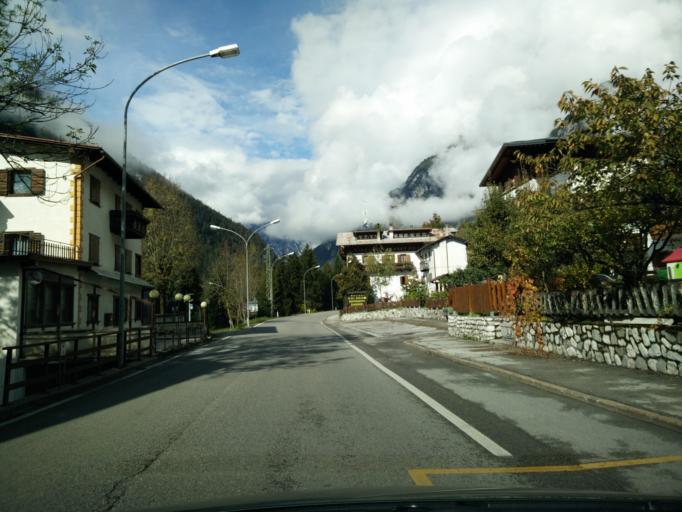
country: IT
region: Veneto
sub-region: Provincia di Belluno
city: Auronzo
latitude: 46.5681
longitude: 12.4026
